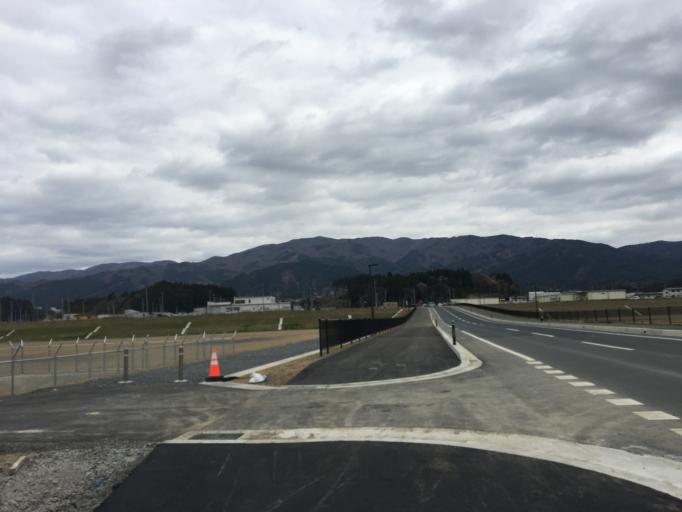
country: JP
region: Iwate
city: Ofunato
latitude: 39.0137
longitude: 141.6237
